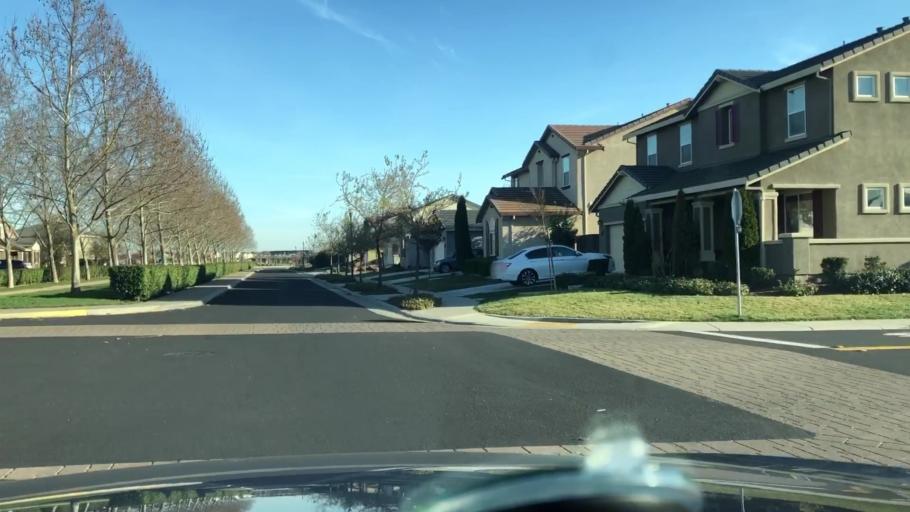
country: US
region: California
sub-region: Sacramento County
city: Laguna
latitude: 38.4023
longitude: -121.4105
